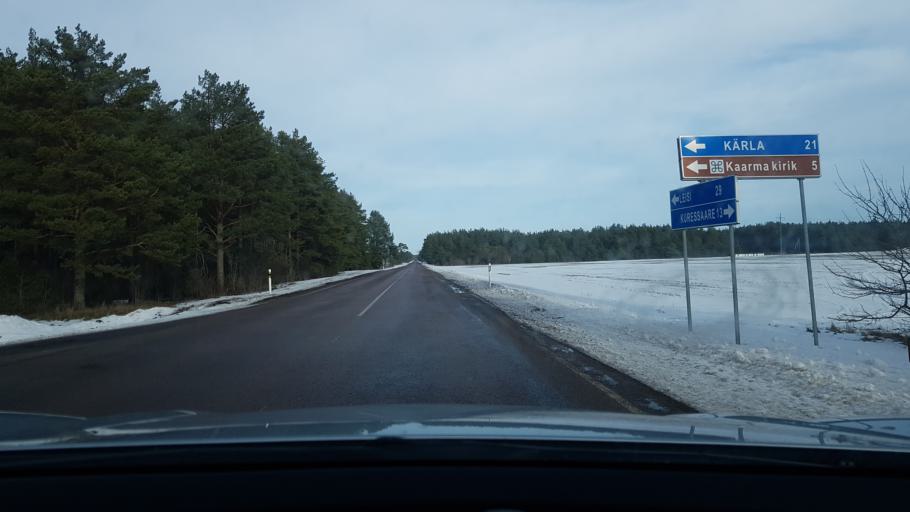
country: EE
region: Saare
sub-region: Kuressaare linn
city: Kuressaare
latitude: 58.3464
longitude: 22.5860
